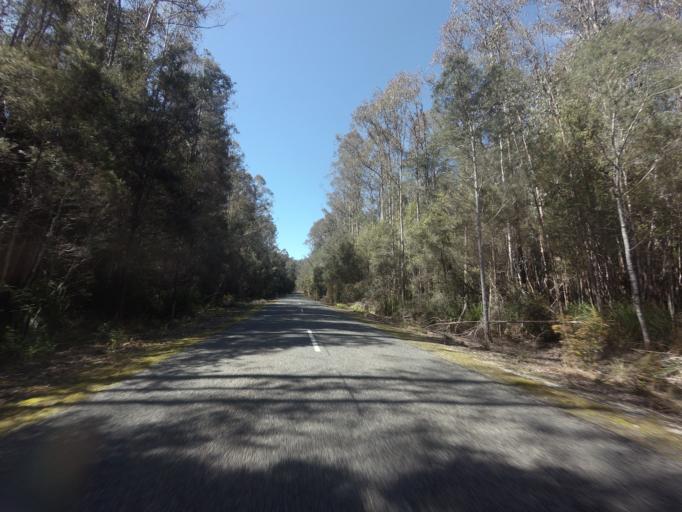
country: AU
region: Tasmania
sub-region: Derwent Valley
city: New Norfolk
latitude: -42.7395
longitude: 146.4206
